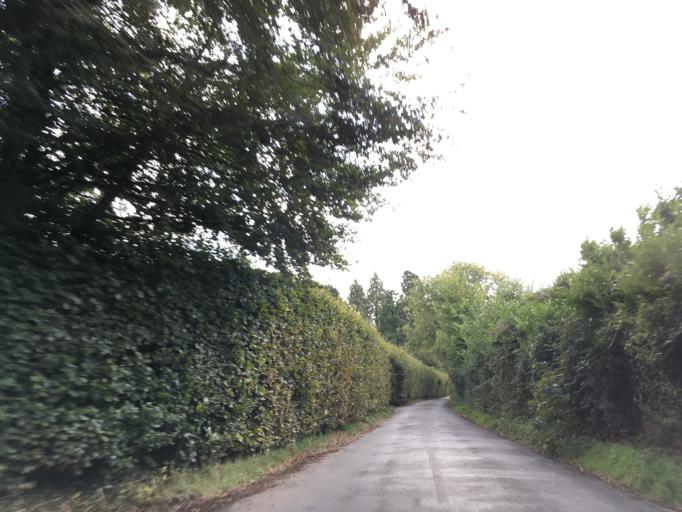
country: GB
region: England
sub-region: Hampshire
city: Andover
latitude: 51.1971
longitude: -1.3830
